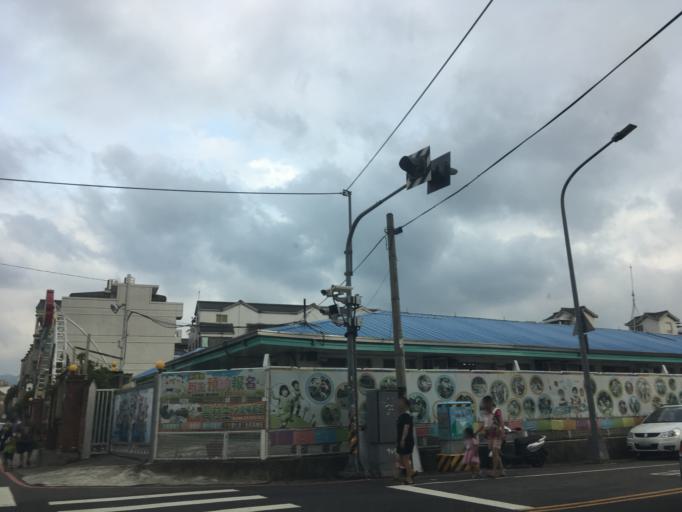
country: TW
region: Taiwan
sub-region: Taichung City
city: Taichung
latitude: 24.1696
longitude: 120.7084
